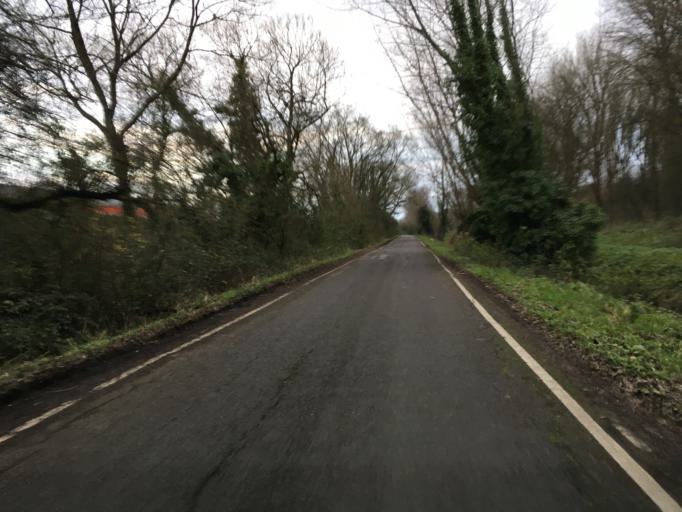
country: GB
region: Wales
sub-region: Newport
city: Bishton
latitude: 51.5755
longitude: -2.8697
